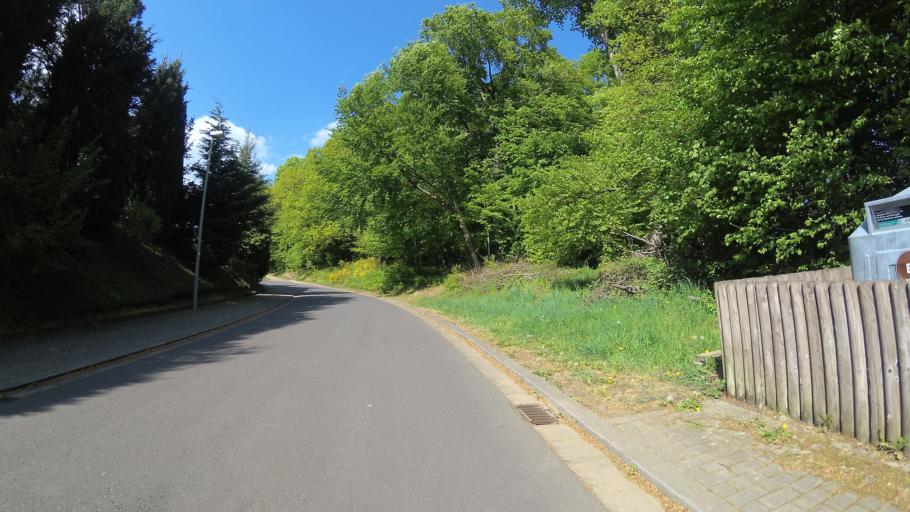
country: DE
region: Rheinland-Pfalz
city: Herchweiler
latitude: 49.4889
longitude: 7.2499
